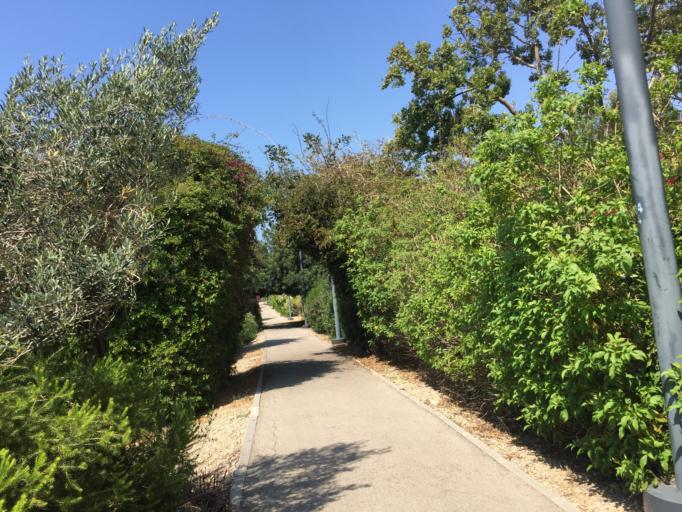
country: IL
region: Haifa
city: Qesarya
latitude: 32.4944
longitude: 34.9042
